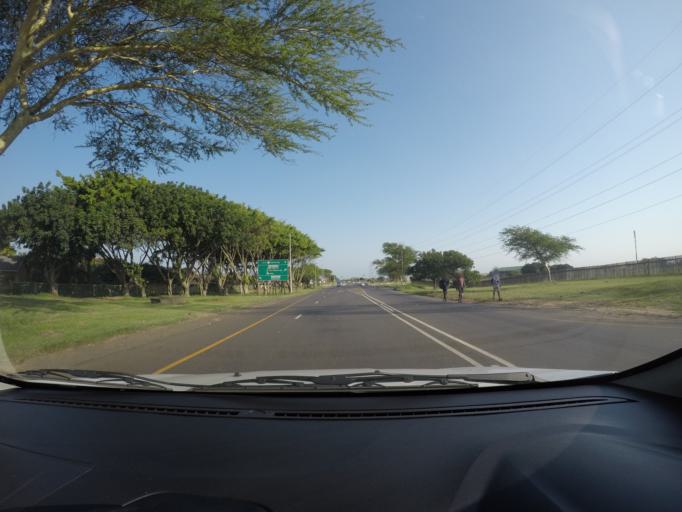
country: ZA
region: KwaZulu-Natal
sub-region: uThungulu District Municipality
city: Richards Bay
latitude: -28.7300
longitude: 32.0379
